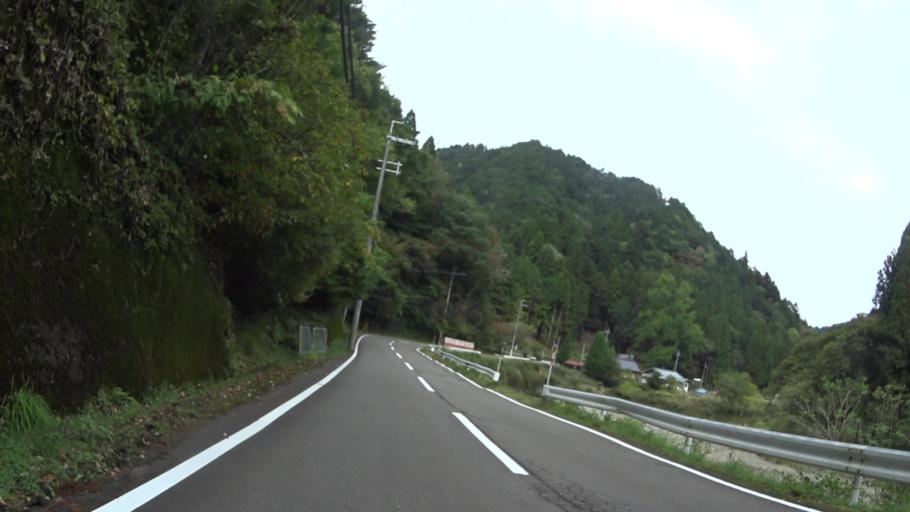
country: JP
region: Shiga Prefecture
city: Kitahama
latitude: 35.2180
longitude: 135.7775
